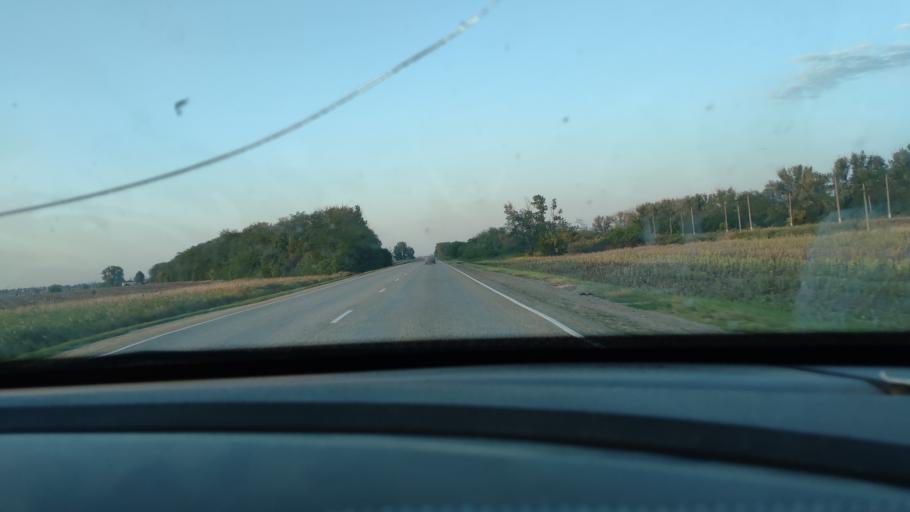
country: RU
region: Krasnodarskiy
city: Starominskaya
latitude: 46.4409
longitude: 39.0229
